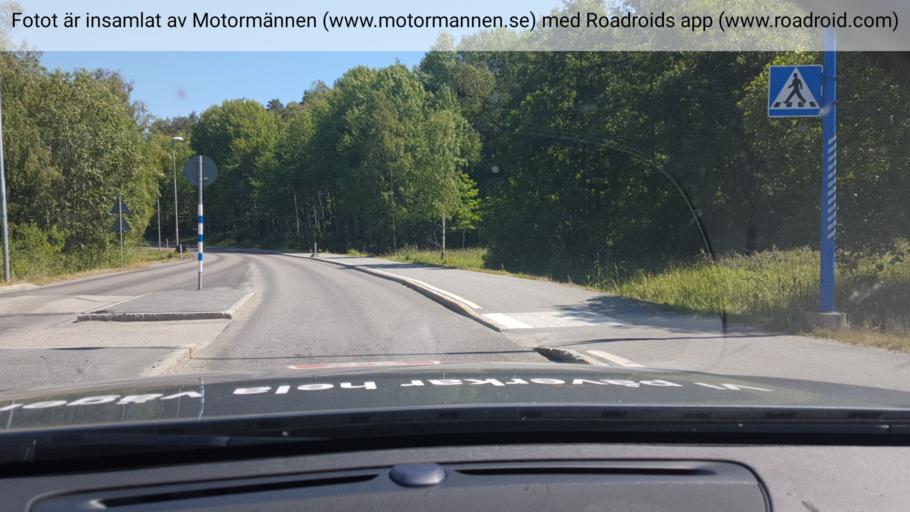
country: SE
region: Stockholm
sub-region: Haninge Kommun
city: Haninge
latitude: 59.1880
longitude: 18.1591
